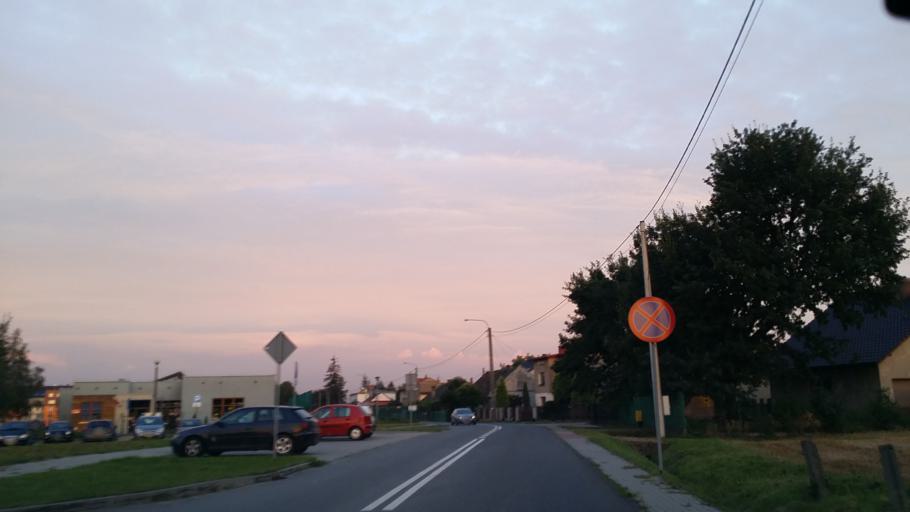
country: PL
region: Lesser Poland Voivodeship
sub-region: Powiat oswiecimski
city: Oswiecim
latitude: 50.0256
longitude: 19.2184
